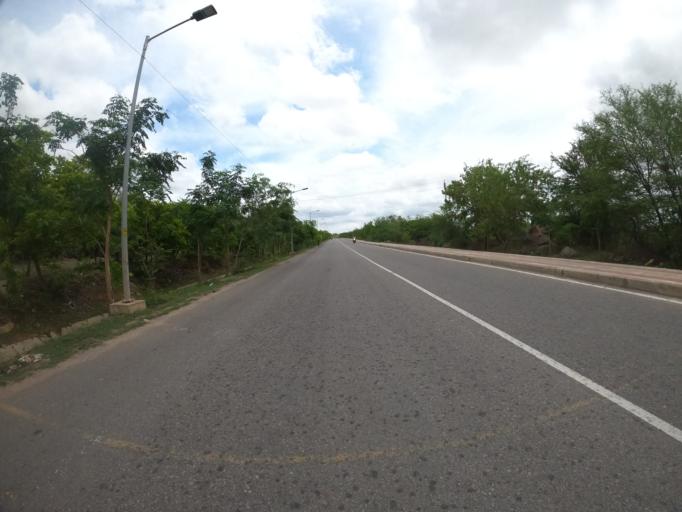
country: IN
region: Telangana
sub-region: Hyderabad
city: Hyderabad
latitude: 17.3683
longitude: 78.3516
